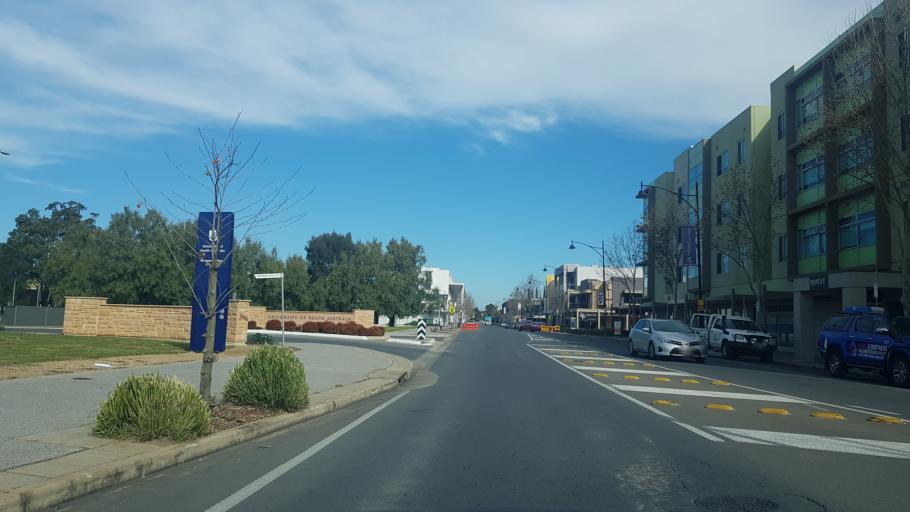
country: AU
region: South Australia
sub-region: Salisbury
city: Ingle Farm
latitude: -34.8065
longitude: 138.6171
